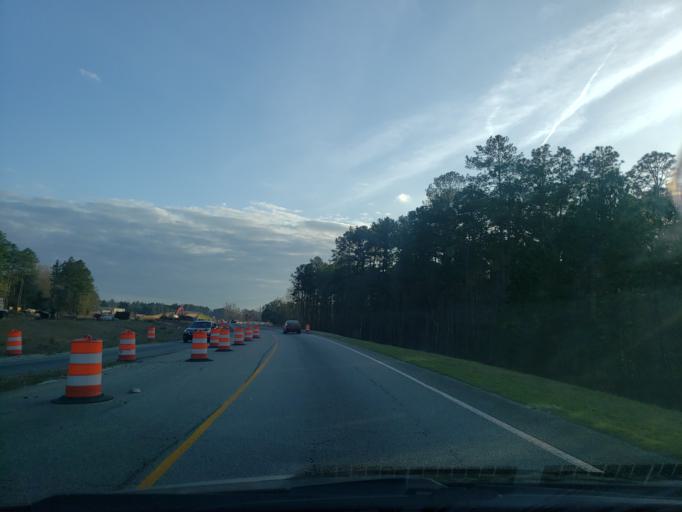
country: US
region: Georgia
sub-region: Chatham County
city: Bloomingdale
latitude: 32.1428
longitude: -81.3082
